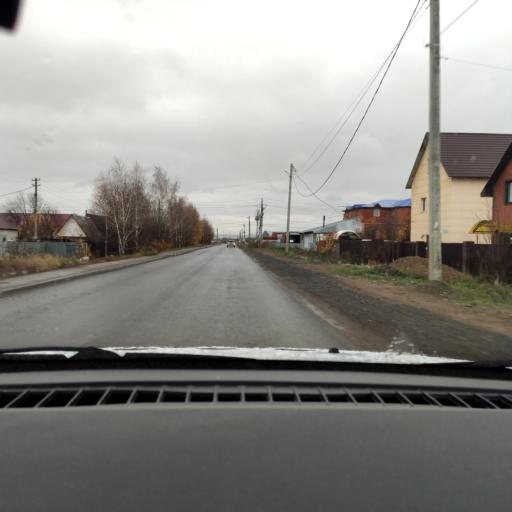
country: RU
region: Perm
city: Kultayevo
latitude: 57.8998
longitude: 55.9603
